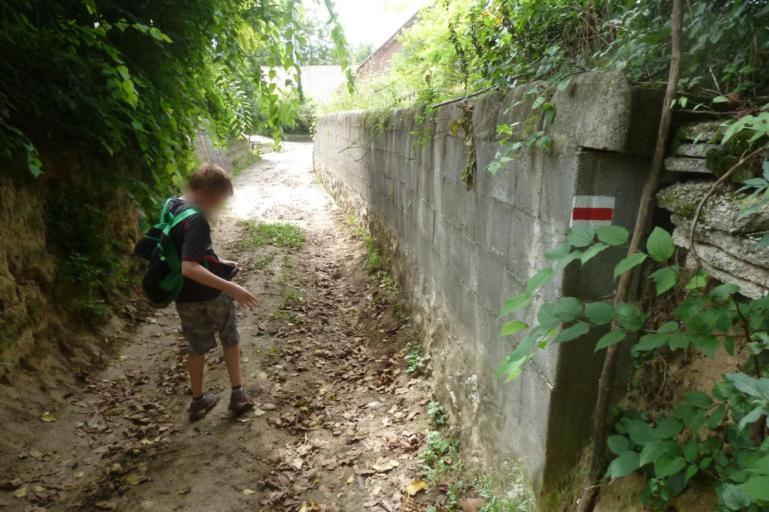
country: HU
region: Baranya
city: Siklos
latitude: 45.8782
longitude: 18.2762
